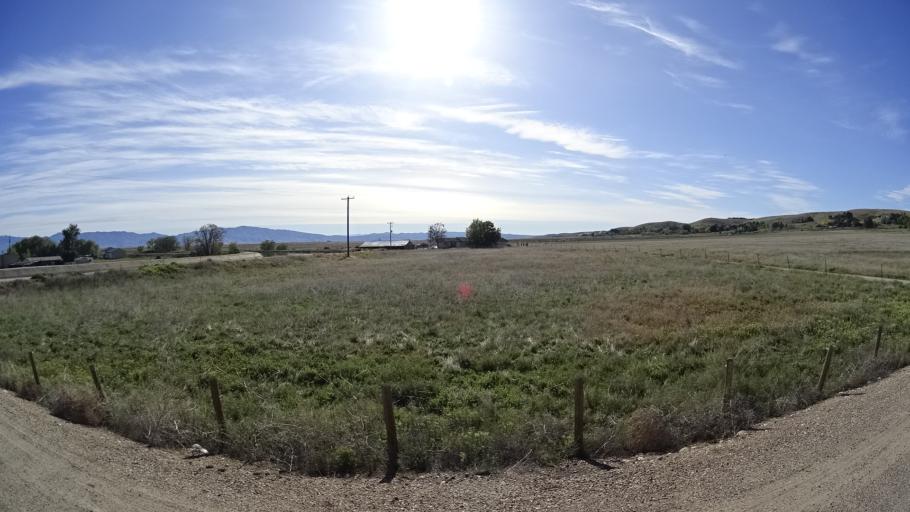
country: US
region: Idaho
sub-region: Ada County
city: Garden City
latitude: 43.5284
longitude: -116.2743
